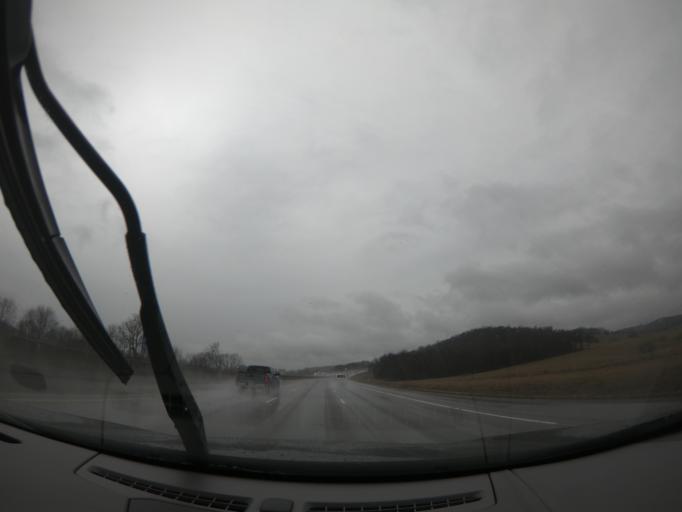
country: US
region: Kentucky
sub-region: Barren County
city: Cave City
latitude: 37.1279
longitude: -85.9873
